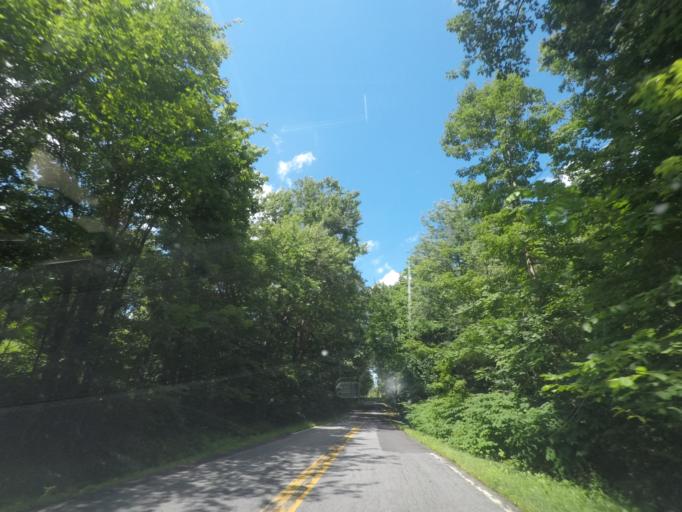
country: US
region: New York
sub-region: Albany County
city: Voorheesville
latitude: 42.7155
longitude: -73.9594
